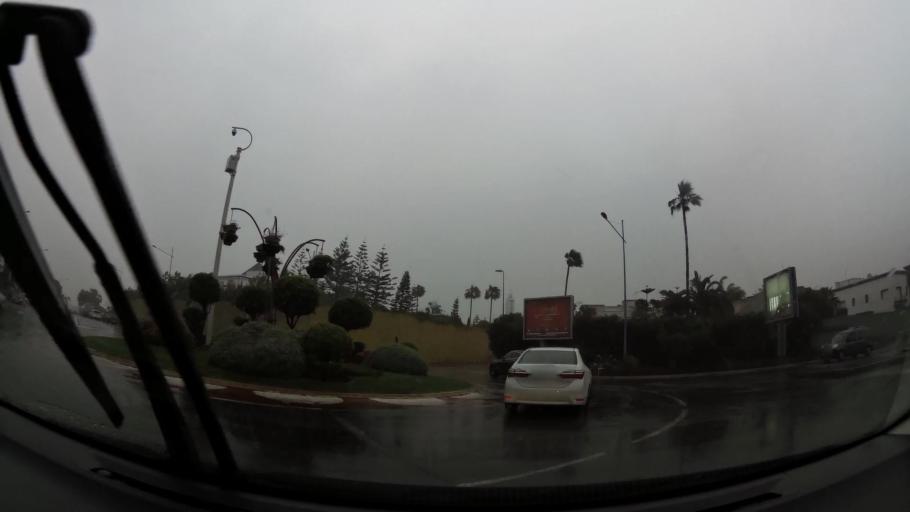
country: MA
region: Grand Casablanca
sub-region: Casablanca
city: Casablanca
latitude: 33.5938
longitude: -7.6670
